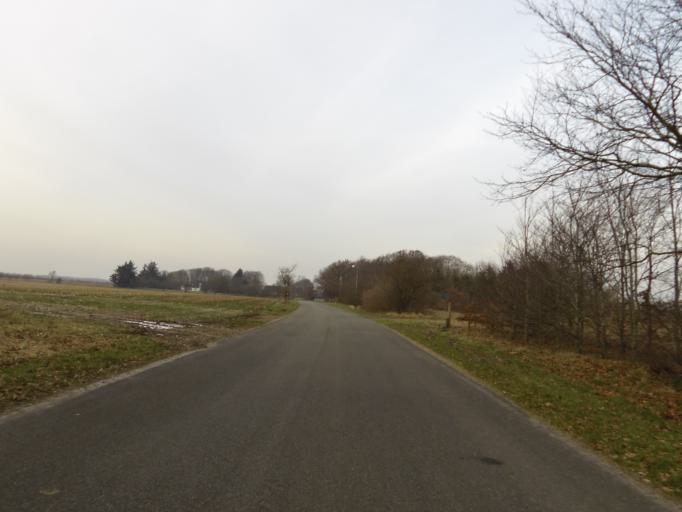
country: DK
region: South Denmark
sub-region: Esbjerg Kommune
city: Ribe
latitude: 55.3340
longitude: 8.8867
